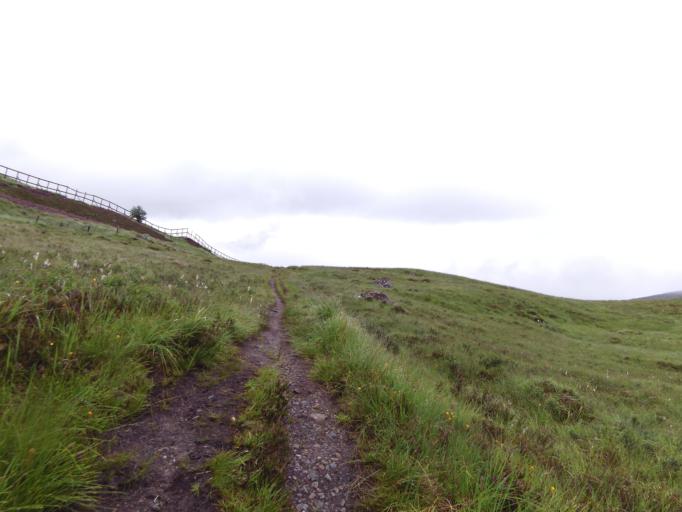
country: GB
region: Scotland
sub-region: Highland
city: Spean Bridge
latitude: 56.7733
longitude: -4.7122
